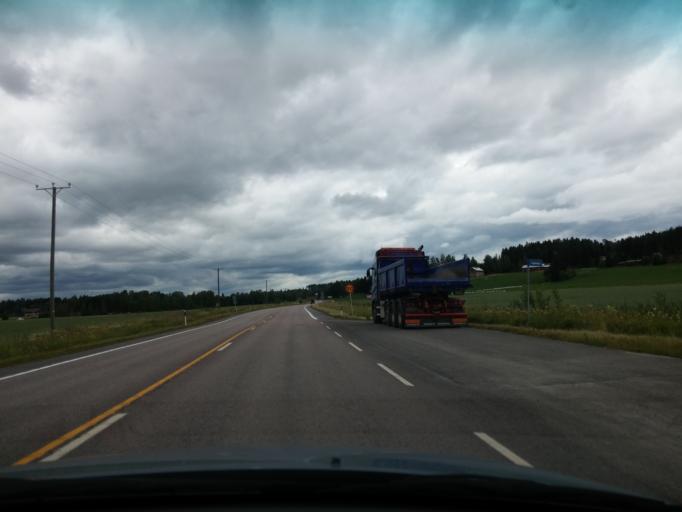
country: FI
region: Uusimaa
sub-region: Porvoo
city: Askola
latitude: 60.4537
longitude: 25.5829
